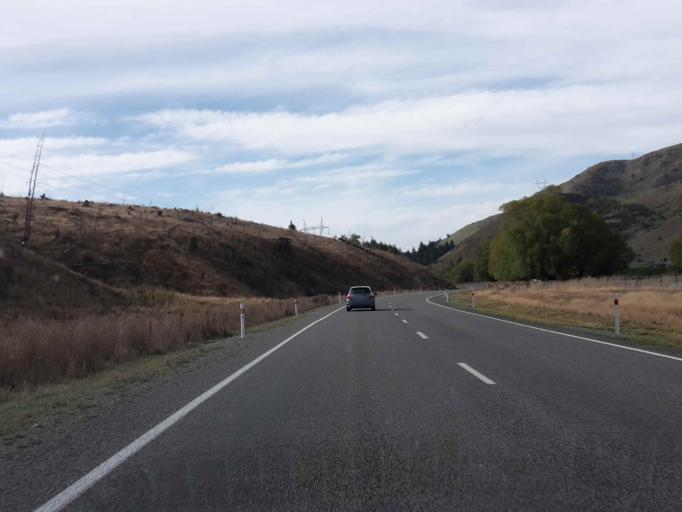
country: NZ
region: Canterbury
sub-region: Timaru District
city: Pleasant Point
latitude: -44.0712
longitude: 170.6670
